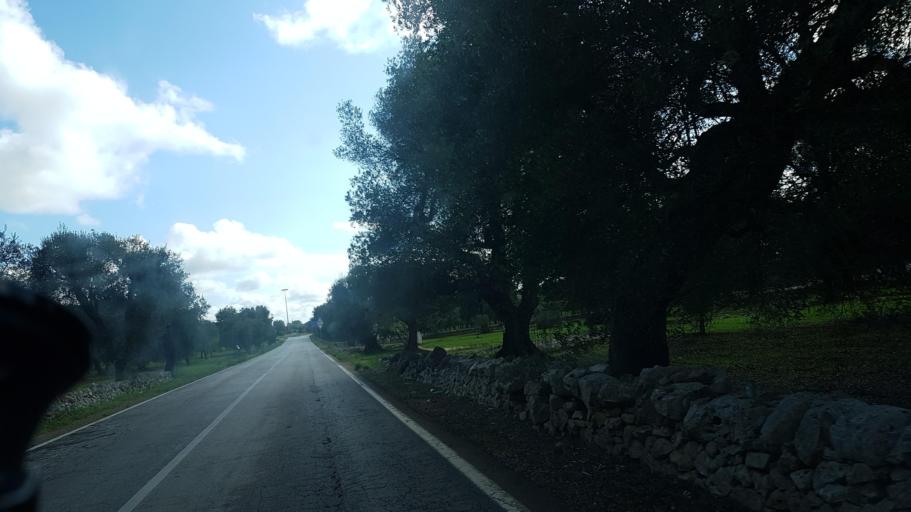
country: IT
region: Apulia
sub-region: Provincia di Brindisi
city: San Michele Salentino
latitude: 40.6489
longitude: 17.6066
